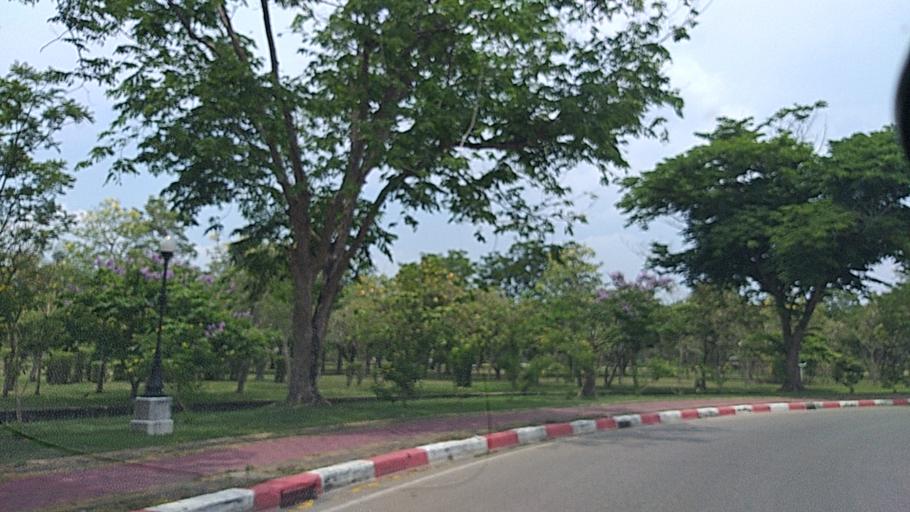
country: TH
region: Bangkok
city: Thawi Watthana
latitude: 13.7752
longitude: 100.3253
